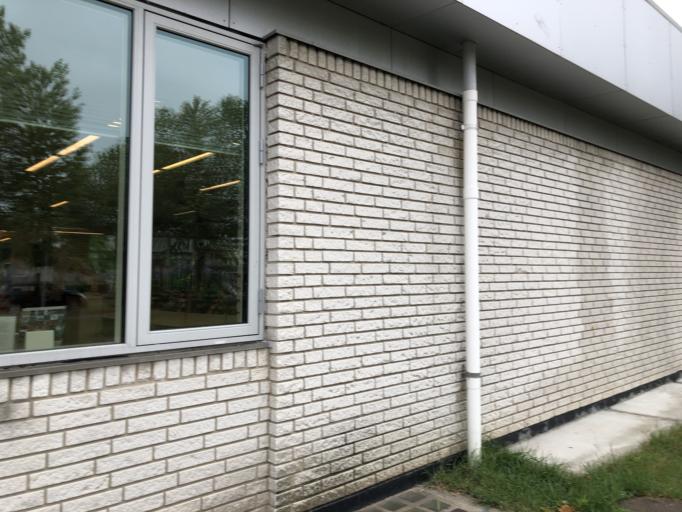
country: DK
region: Capital Region
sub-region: Bornholm Kommune
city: Ronne
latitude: 55.1017
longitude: 14.7080
